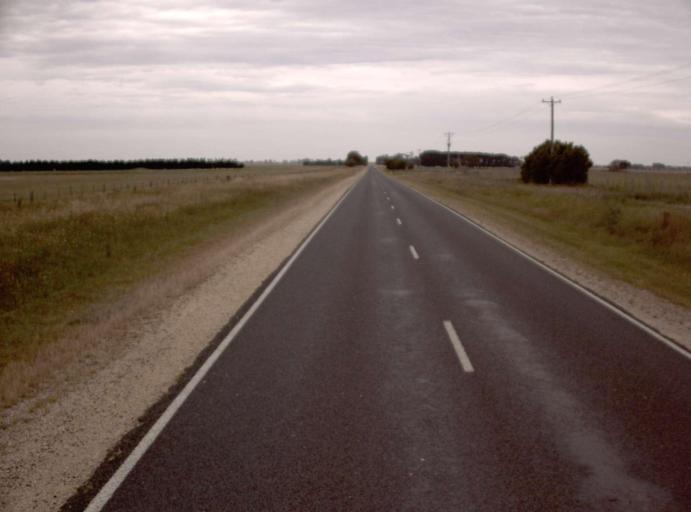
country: AU
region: Victoria
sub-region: Wellington
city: Sale
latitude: -38.1734
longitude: 147.1830
